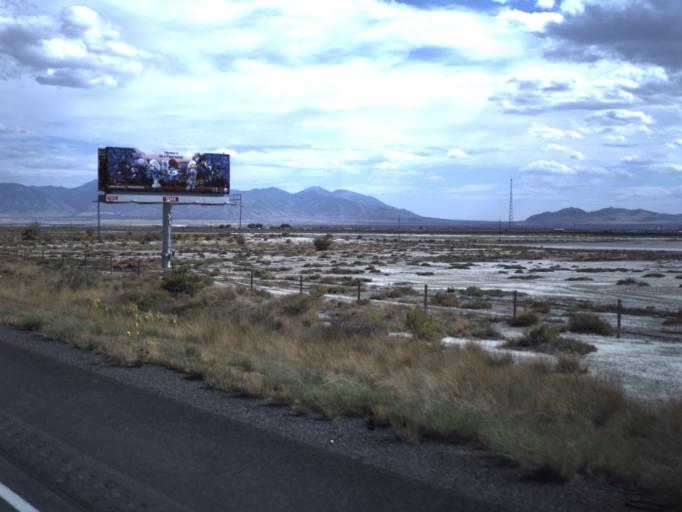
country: US
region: Utah
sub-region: Tooele County
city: Grantsville
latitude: 40.6890
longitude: -112.4585
